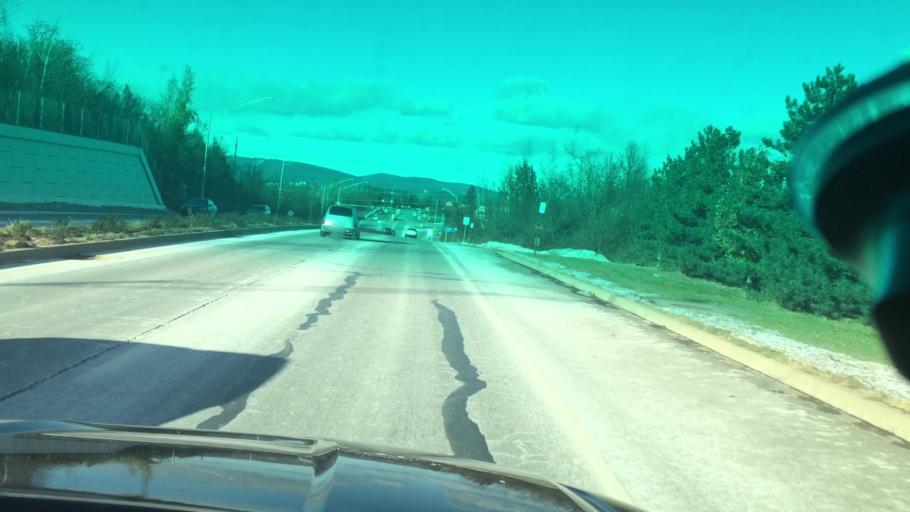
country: US
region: Pennsylvania
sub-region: Luzerne County
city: Georgetown
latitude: 41.2410
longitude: -75.8496
